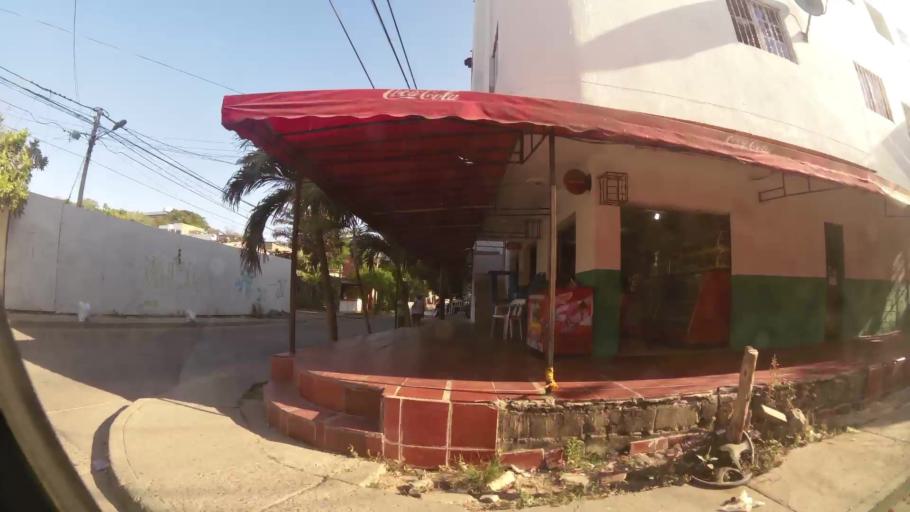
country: CO
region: Bolivar
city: Cartagena
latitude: 10.4016
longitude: -75.5023
